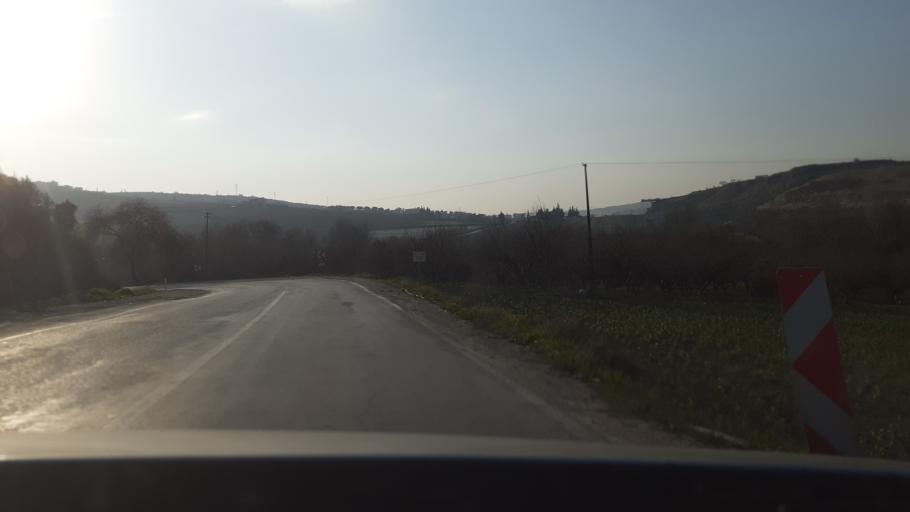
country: TR
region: Hatay
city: Oymakli
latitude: 36.1107
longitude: 36.2761
